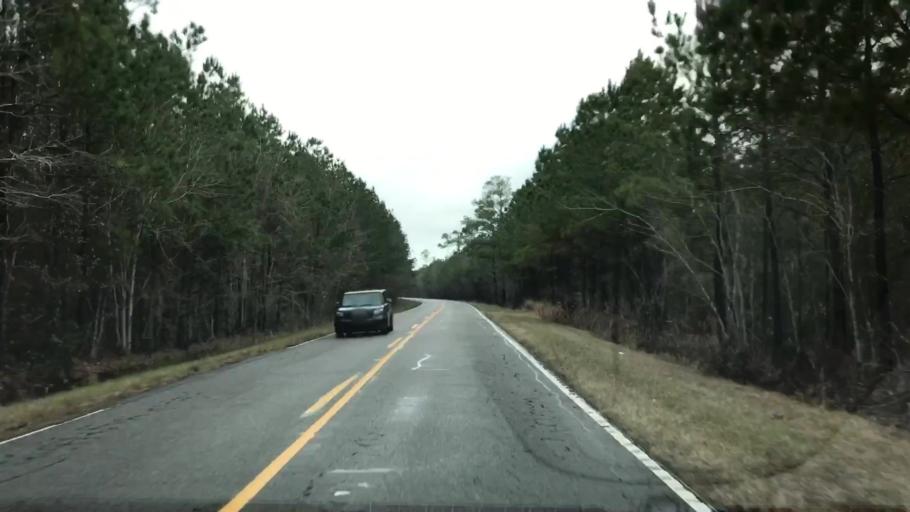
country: US
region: South Carolina
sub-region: Georgetown County
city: Murrells Inlet
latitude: 33.6310
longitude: -79.2490
